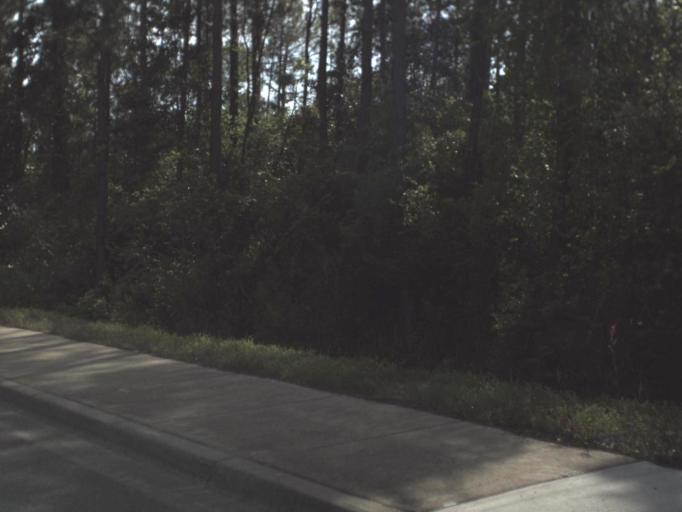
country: US
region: Florida
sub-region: Santa Rosa County
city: Navarre
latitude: 30.4283
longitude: -86.8669
